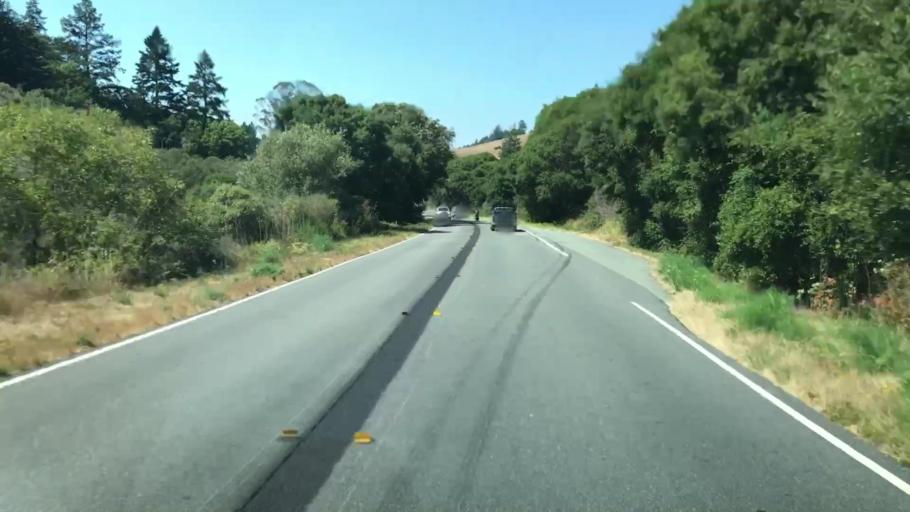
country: US
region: California
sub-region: Marin County
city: Lagunitas-Forest Knolls
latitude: 37.9764
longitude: -122.7331
